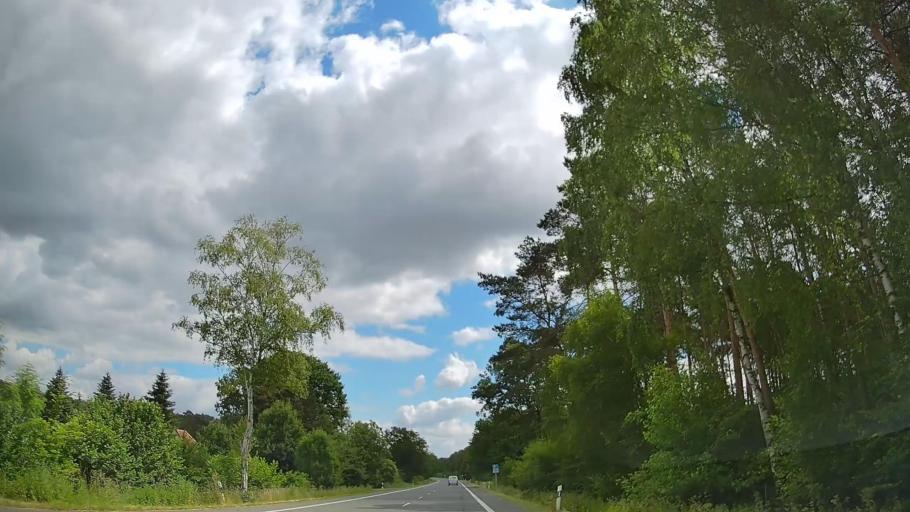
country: DE
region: North Rhine-Westphalia
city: Espelkamp
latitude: 52.3934
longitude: 8.5809
